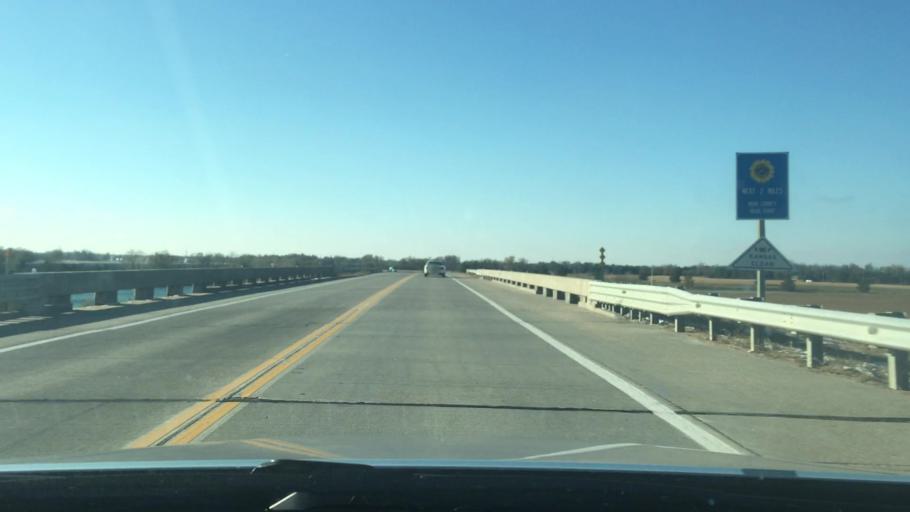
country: US
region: Kansas
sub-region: Reno County
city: Nickerson
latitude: 38.1024
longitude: -98.0144
